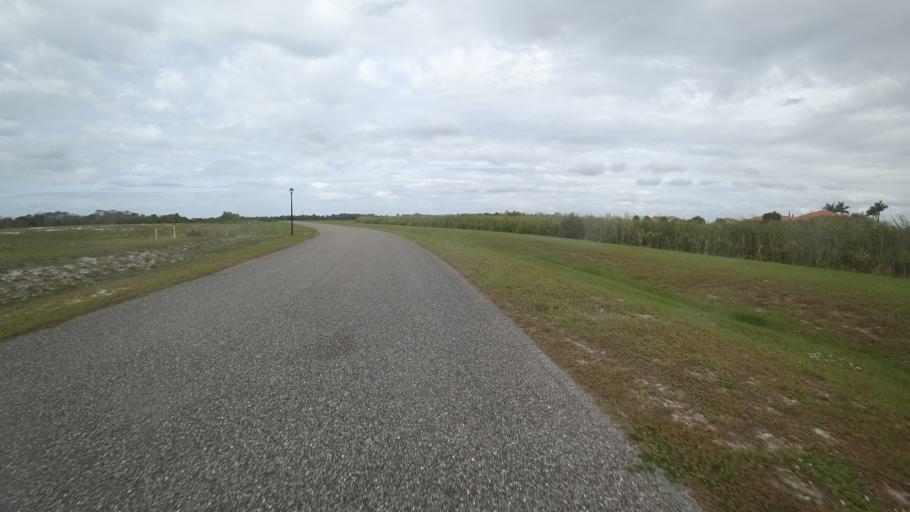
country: US
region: Florida
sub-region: Hillsborough County
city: Wimauma
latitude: 27.6507
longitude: -82.3307
